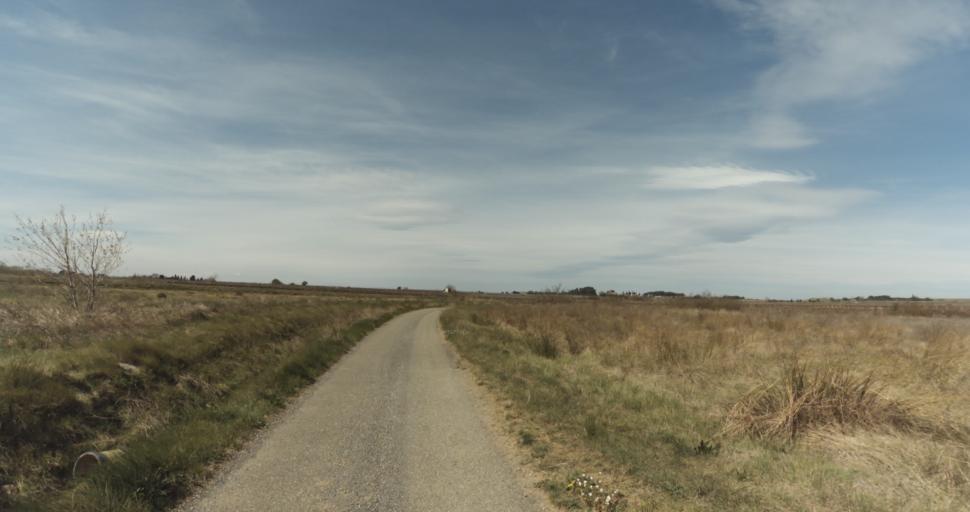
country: FR
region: Languedoc-Roussillon
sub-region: Departement de l'Herault
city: Marseillan
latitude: 43.3721
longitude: 3.5275
